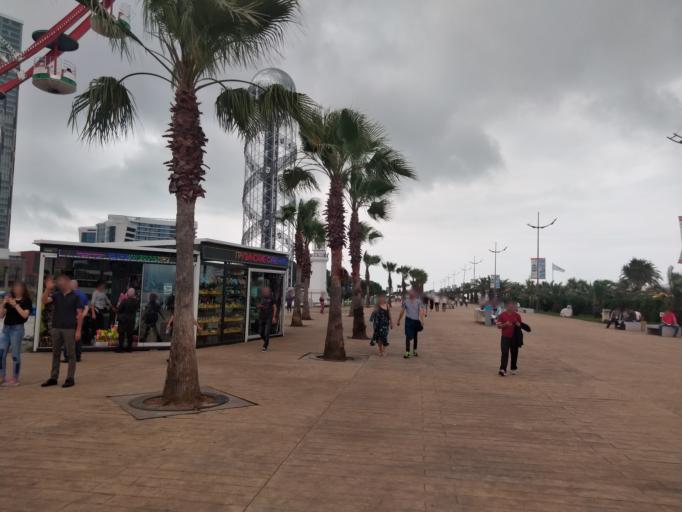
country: GE
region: Ajaria
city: Batumi
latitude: 41.6556
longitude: 41.6428
